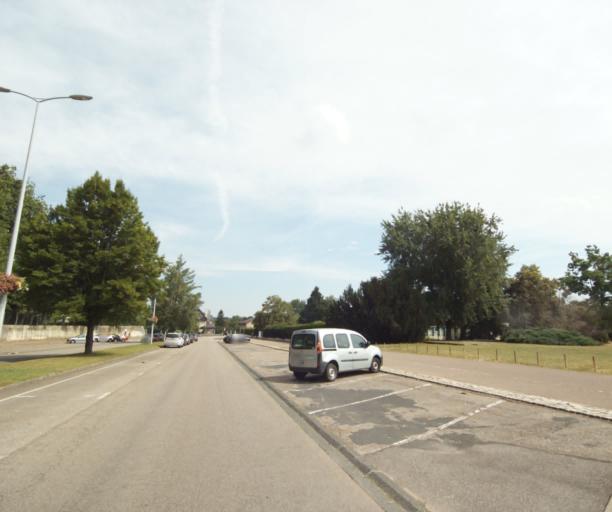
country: FR
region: Lorraine
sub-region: Departement de Meurthe-et-Moselle
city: Luneville
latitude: 48.5954
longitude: 6.5031
